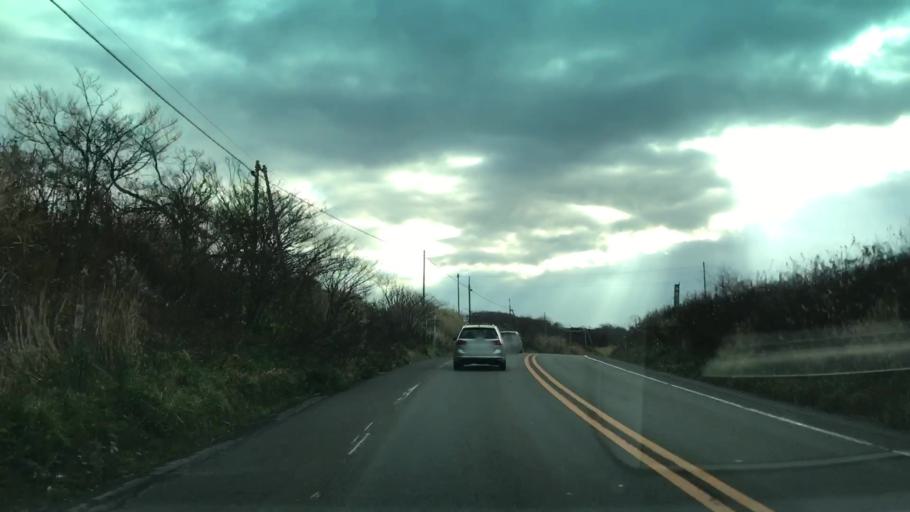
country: JP
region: Hokkaido
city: Shizunai-furukawacho
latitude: 42.4131
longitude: 142.2419
